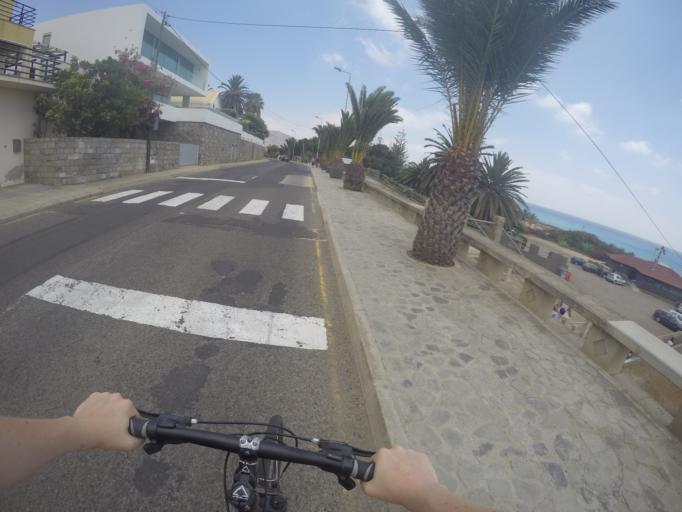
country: PT
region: Madeira
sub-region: Porto Santo
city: Vila de Porto Santo
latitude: 33.0534
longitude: -16.3496
